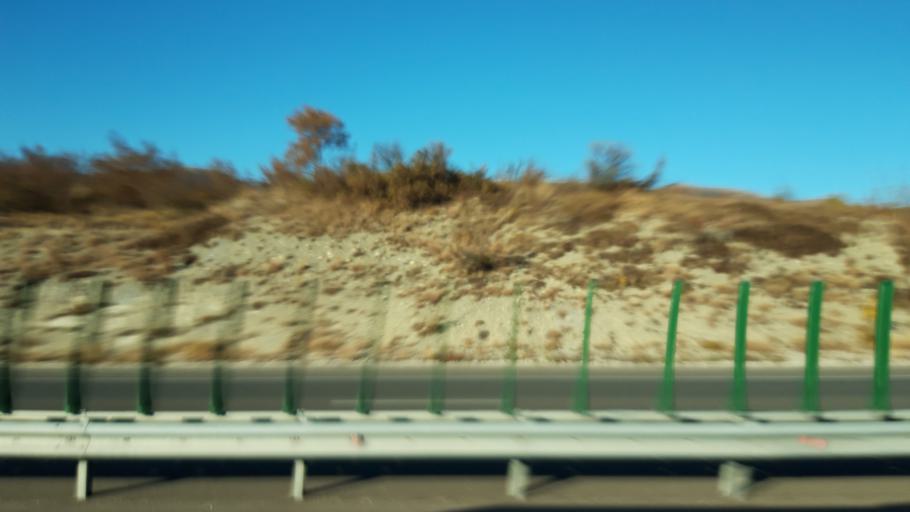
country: RU
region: Krasnodarskiy
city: Kabardinka
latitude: 44.6413
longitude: 37.9769
